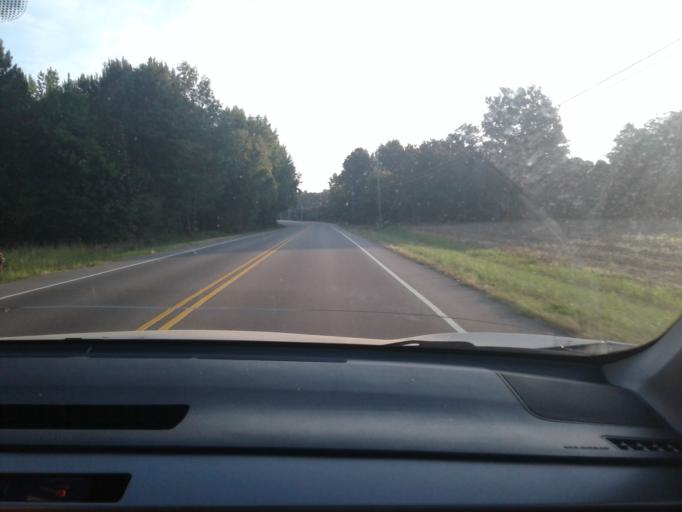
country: US
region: North Carolina
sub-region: Harnett County
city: Lillington
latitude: 35.4642
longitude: -78.8292
